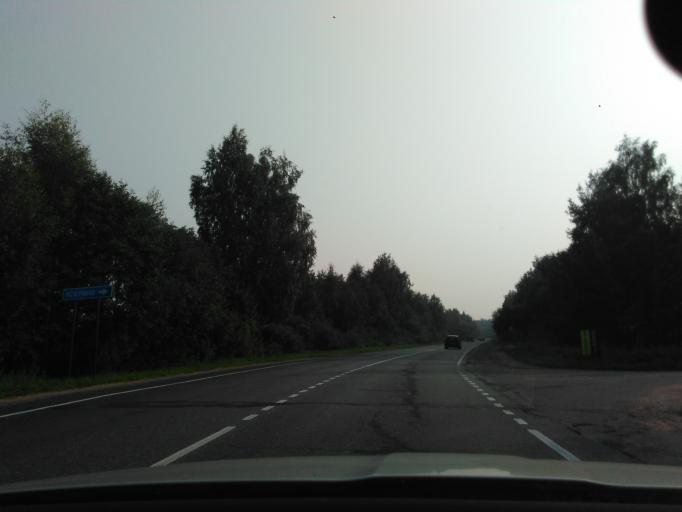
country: RU
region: Tverskaya
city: Zavidovo
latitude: 56.6155
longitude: 36.6407
